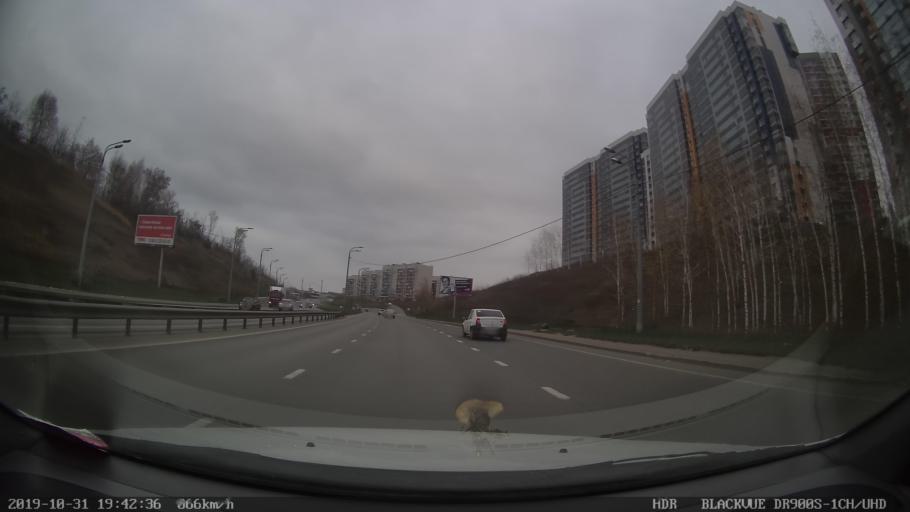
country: RU
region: Tatarstan
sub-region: Gorod Kazan'
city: Kazan
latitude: 55.7671
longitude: 49.1702
